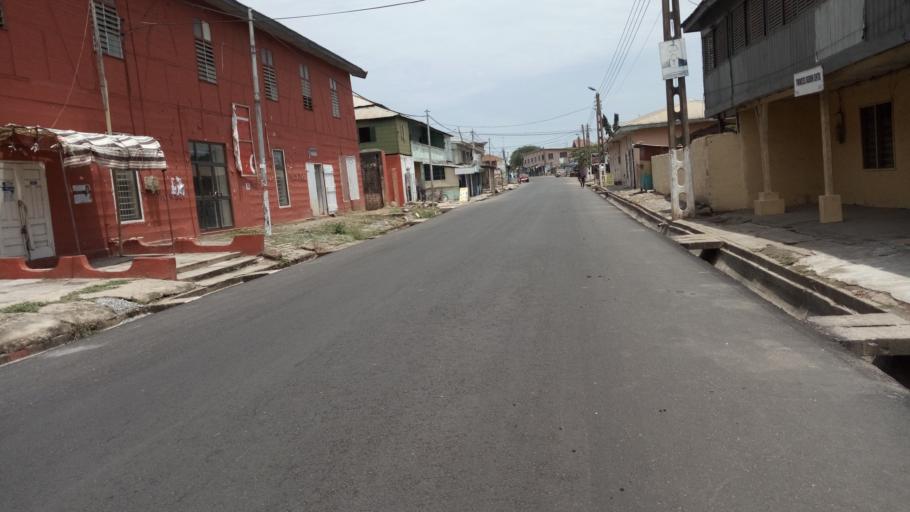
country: GH
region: Central
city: Winneba
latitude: 5.3424
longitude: -0.6260
